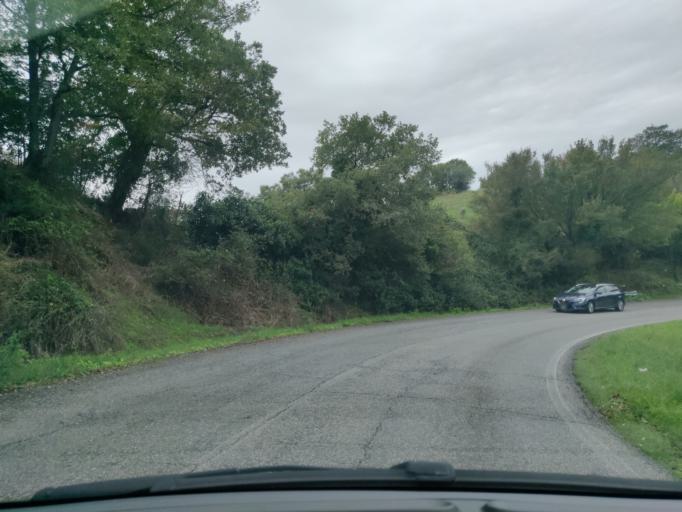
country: IT
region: Latium
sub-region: Citta metropolitana di Roma Capitale
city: Allumiere
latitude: 42.1443
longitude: 11.8833
